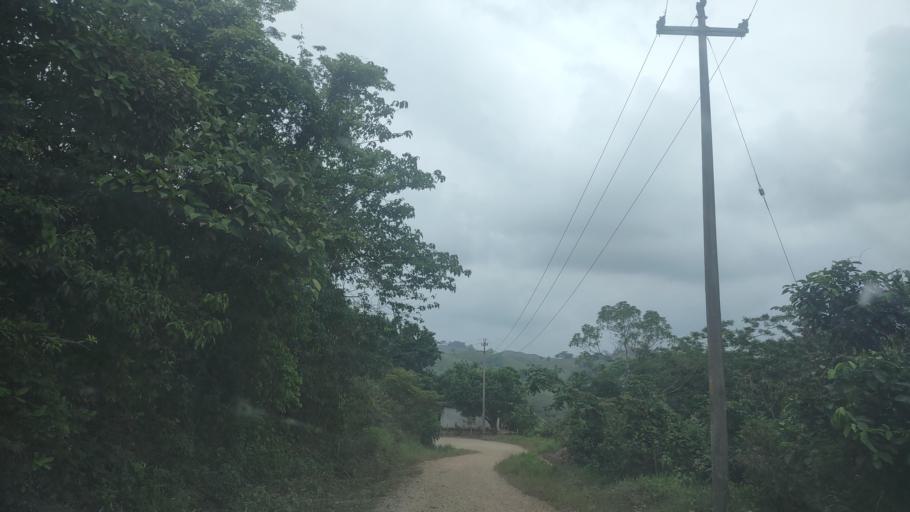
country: MX
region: Tabasco
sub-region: Huimanguillo
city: Francisco Rueda
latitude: 17.4399
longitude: -94.0247
